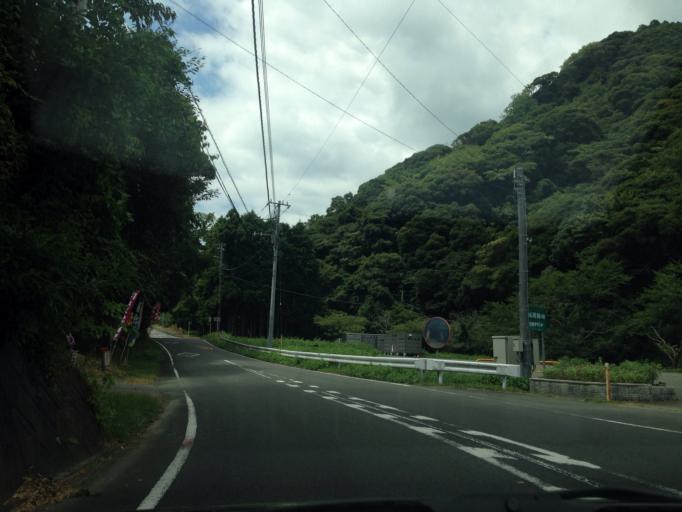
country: JP
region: Shizuoka
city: Shimoda
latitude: 34.6464
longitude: 138.8197
